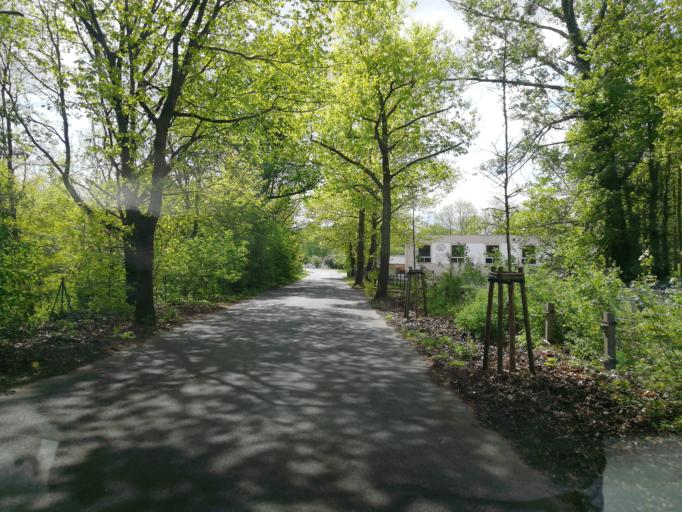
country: DE
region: Brandenburg
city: Lauchhammer
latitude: 51.5072
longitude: 13.7993
